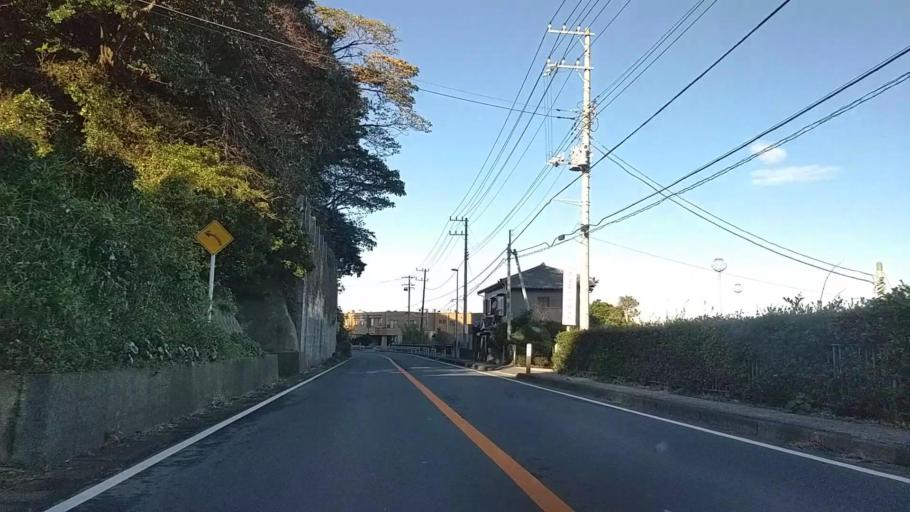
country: JP
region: Chiba
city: Futtsu
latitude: 35.2038
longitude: 139.8352
